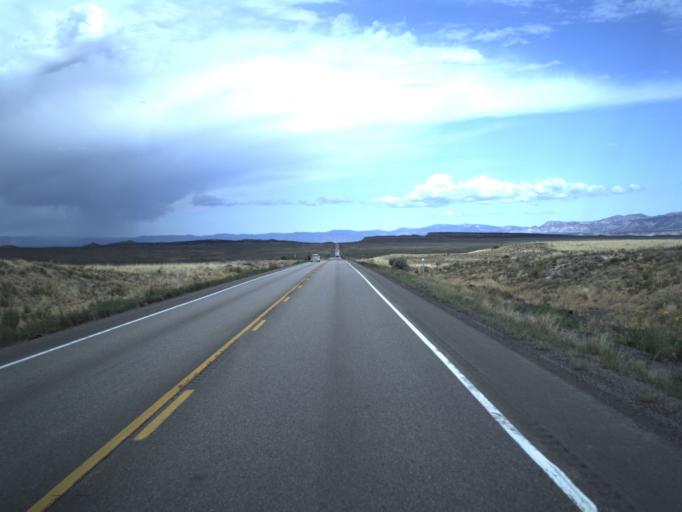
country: US
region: Utah
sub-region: Carbon County
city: East Carbon City
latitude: 39.5180
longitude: -110.5552
